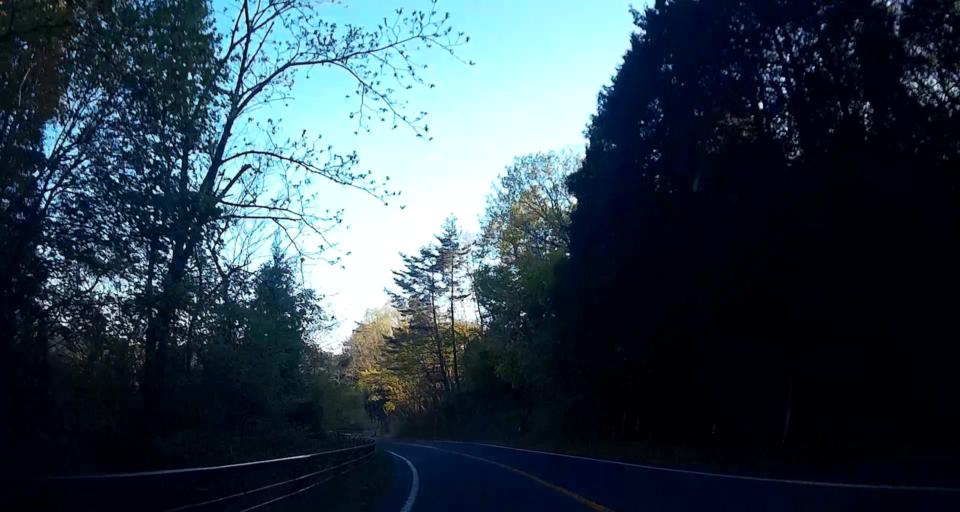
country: JP
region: Iwate
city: Miyako
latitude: 39.6539
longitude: 141.9619
